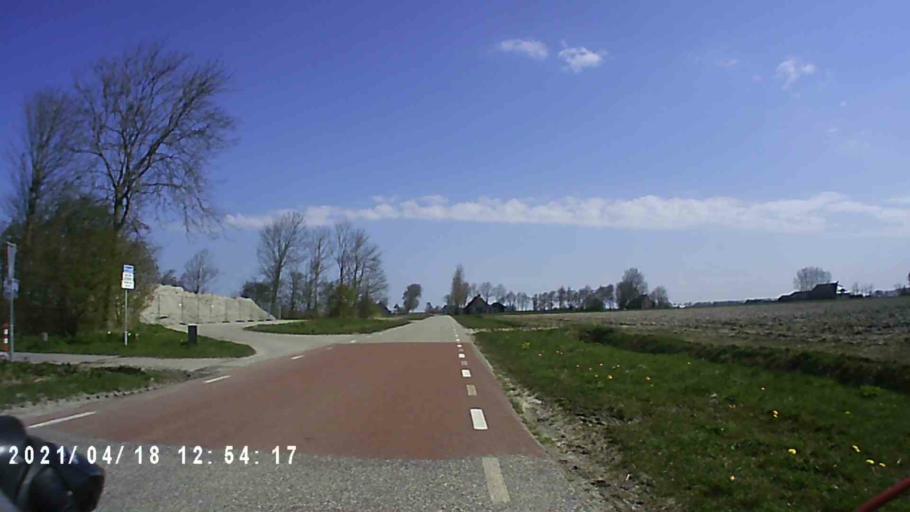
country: NL
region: Friesland
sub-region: Gemeente Dongeradeel
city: Anjum
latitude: 53.3851
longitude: 6.0698
